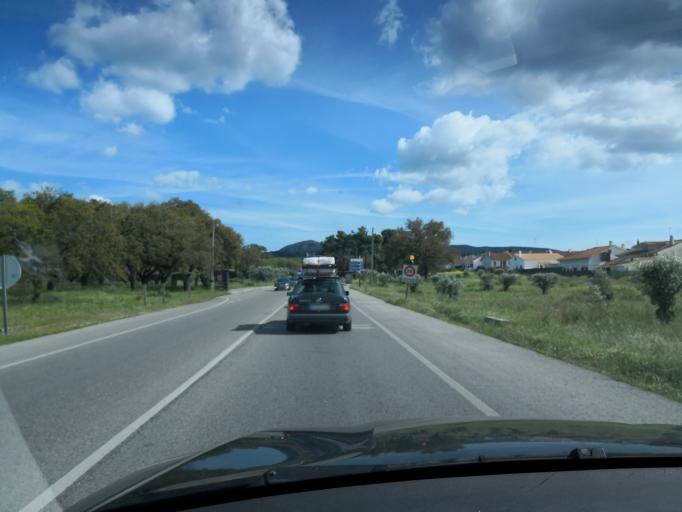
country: PT
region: Setubal
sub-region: Palmela
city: Quinta do Anjo
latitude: 38.5264
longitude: -9.0185
